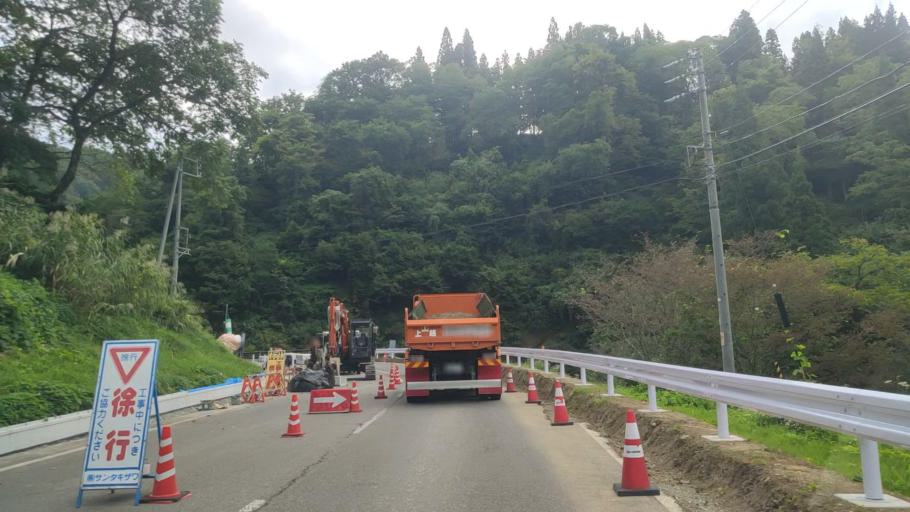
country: JP
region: Nagano
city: Iiyama
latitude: 36.9030
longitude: 138.3150
